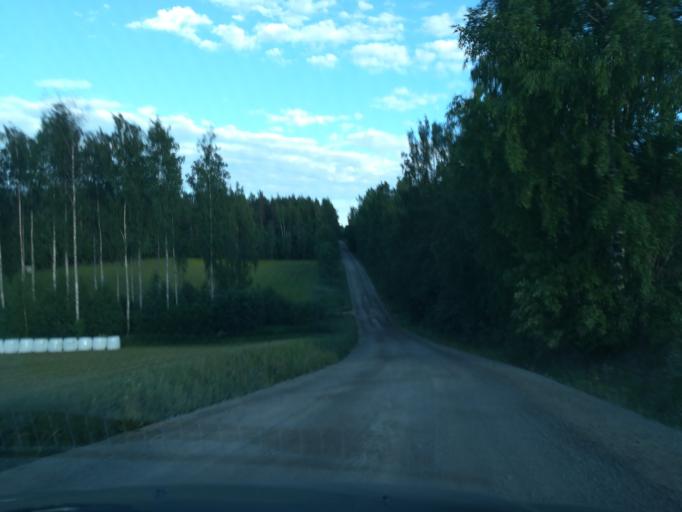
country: FI
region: Southern Savonia
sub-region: Mikkeli
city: Puumala
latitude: 61.5881
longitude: 28.1169
